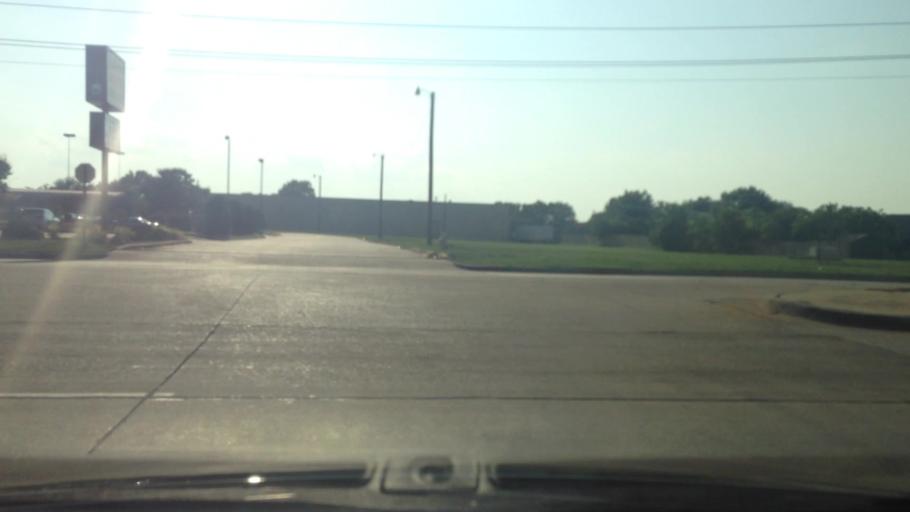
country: US
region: Texas
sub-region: Tarrant County
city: Edgecliff Village
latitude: 32.6501
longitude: -97.3483
